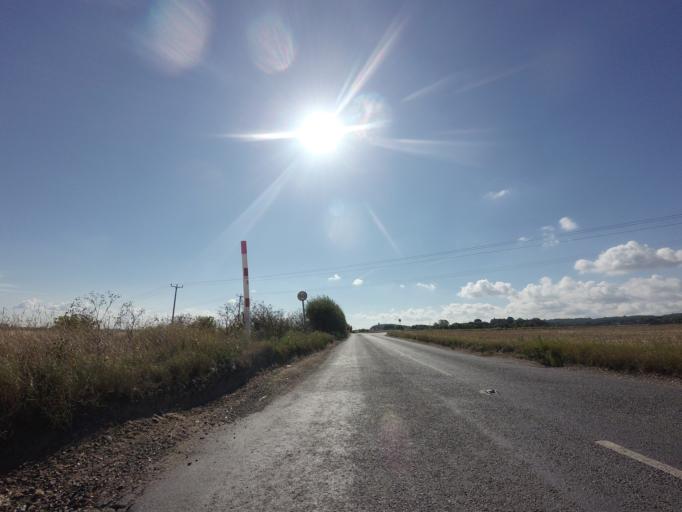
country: GB
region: England
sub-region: Medway
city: Cuxton
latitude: 51.4291
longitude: 0.4345
